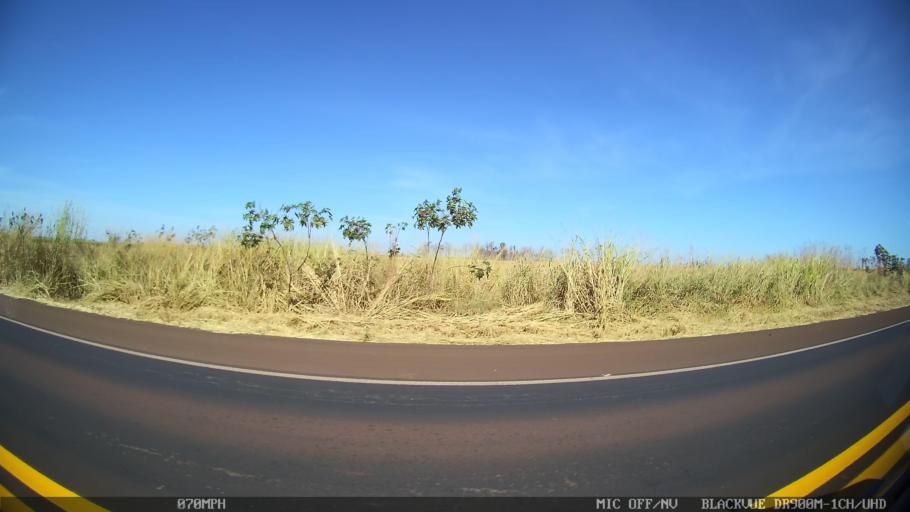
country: BR
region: Sao Paulo
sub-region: Barretos
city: Barretos
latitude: -20.4843
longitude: -48.5104
